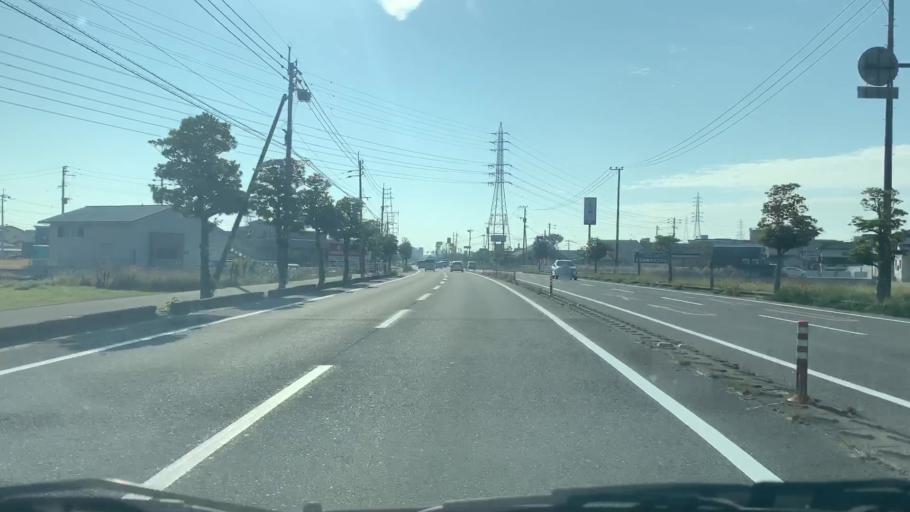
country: JP
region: Saga Prefecture
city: Saga-shi
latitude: 33.2971
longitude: 130.2819
